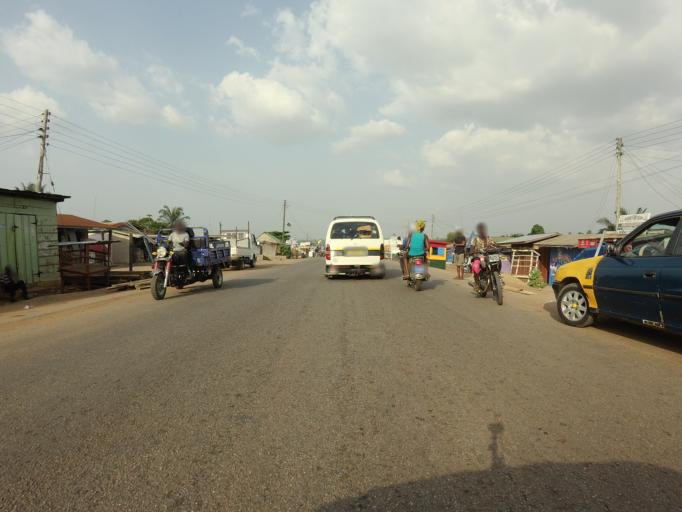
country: GH
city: Akropong
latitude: 6.2514
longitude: 0.1316
